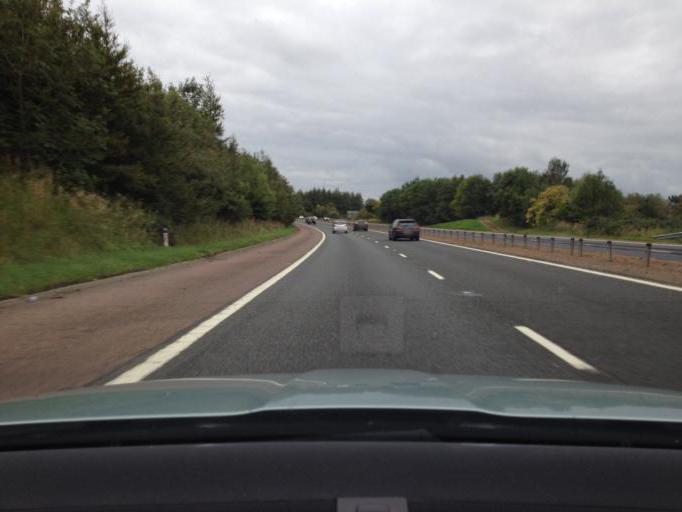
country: GB
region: Scotland
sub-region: Fife
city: Kelty
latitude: 56.1161
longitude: -3.3937
